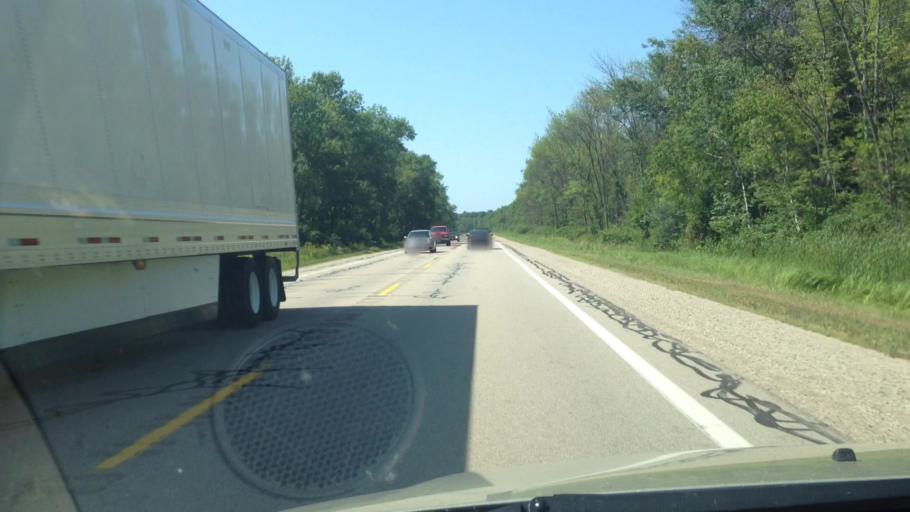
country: US
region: Michigan
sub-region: Menominee County
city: Menominee
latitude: 45.3295
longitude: -87.4239
